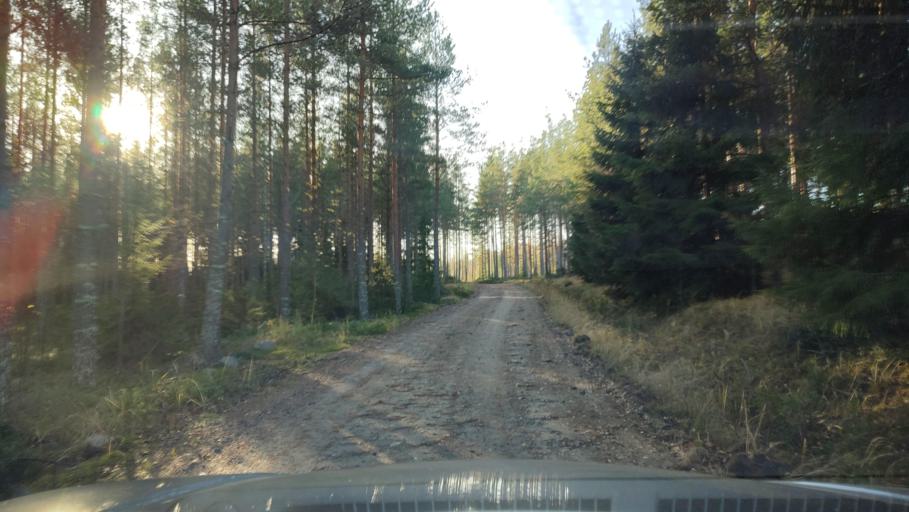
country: FI
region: Southern Ostrobothnia
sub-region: Suupohja
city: Karijoki
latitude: 62.2152
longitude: 21.6277
